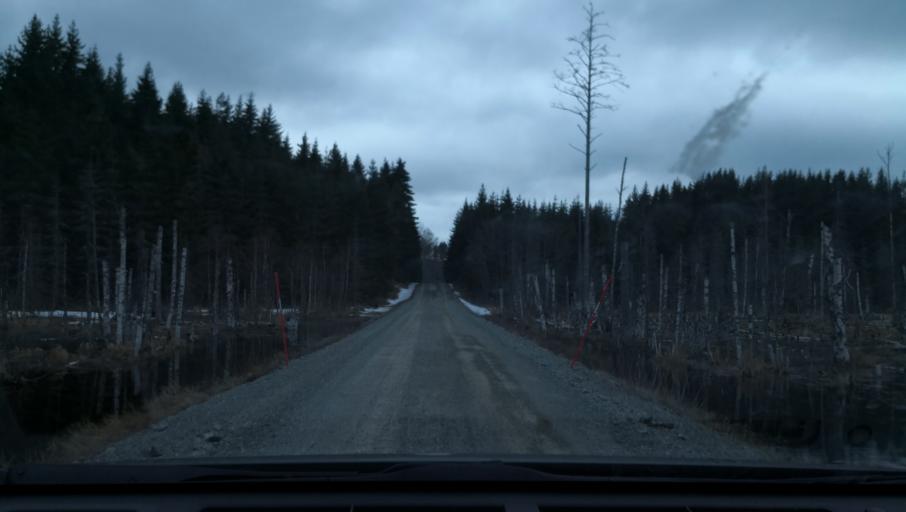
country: SE
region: OErebro
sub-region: Lindesbergs Kommun
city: Fellingsbro
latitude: 59.6115
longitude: 15.6022
